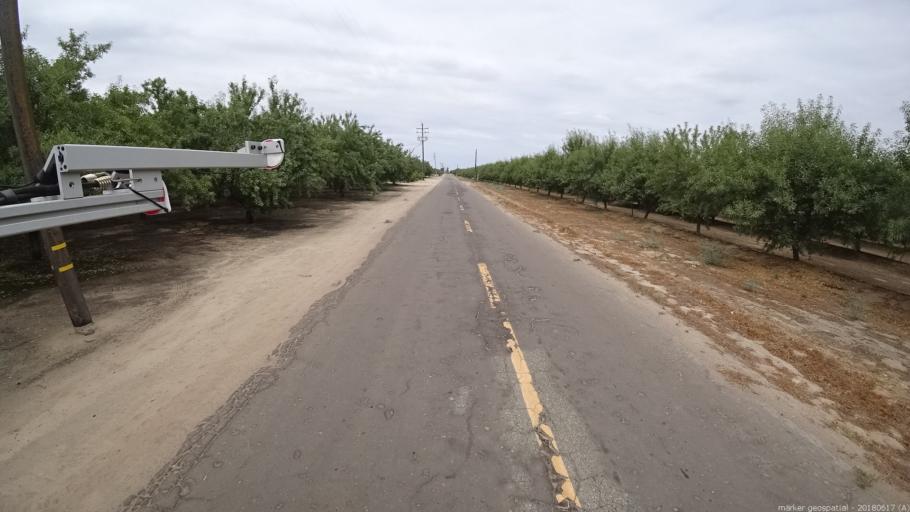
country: US
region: California
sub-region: Madera County
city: Fairmead
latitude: 37.0038
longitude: -120.2213
